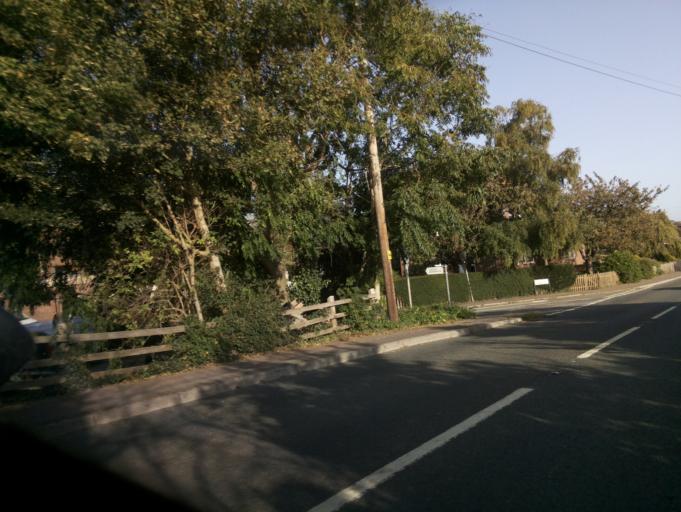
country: GB
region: England
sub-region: Gloucestershire
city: Tewkesbury
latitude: 51.9542
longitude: -2.2377
